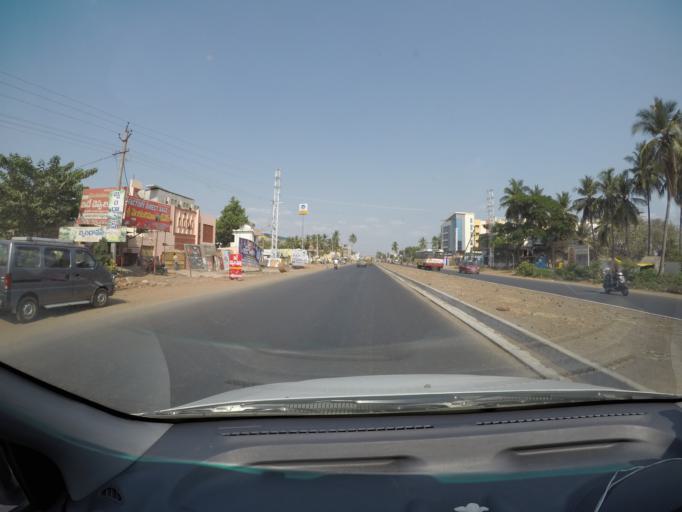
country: IN
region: Andhra Pradesh
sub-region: Krishna
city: Yanamalakuduru
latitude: 16.4742
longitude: 80.7125
